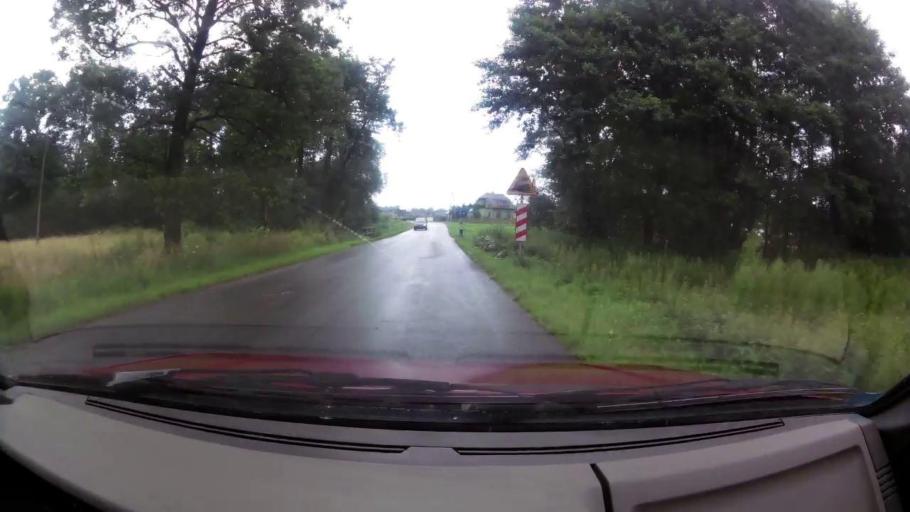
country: PL
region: West Pomeranian Voivodeship
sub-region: Koszalin
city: Koszalin
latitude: 54.1328
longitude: 16.1187
